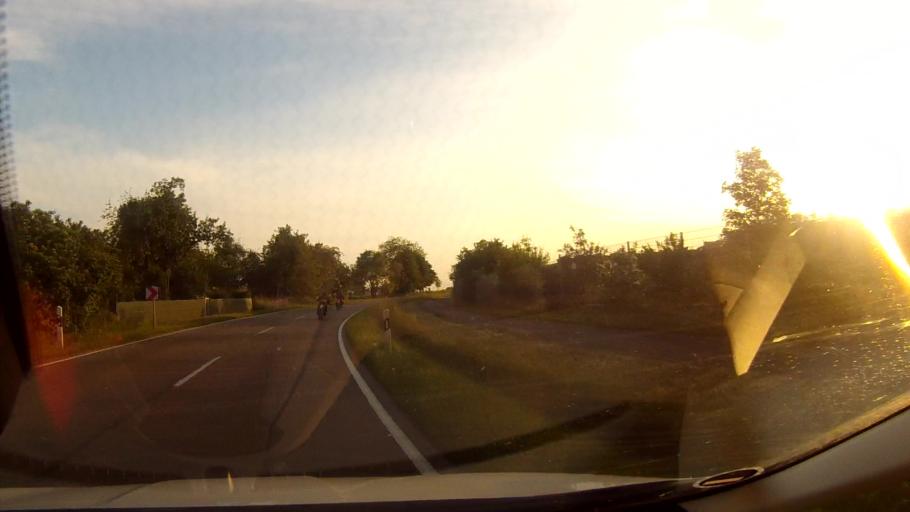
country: DE
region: Baden-Wuerttemberg
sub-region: Tuebingen Region
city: Staig
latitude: 48.2987
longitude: 10.0132
